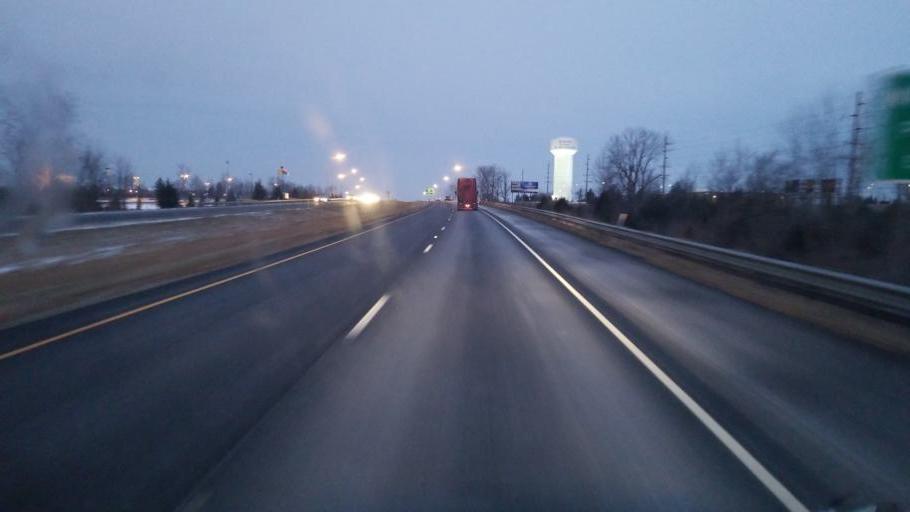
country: US
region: Indiana
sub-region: Wayne County
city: Richmond
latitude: 39.8727
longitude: -84.8778
